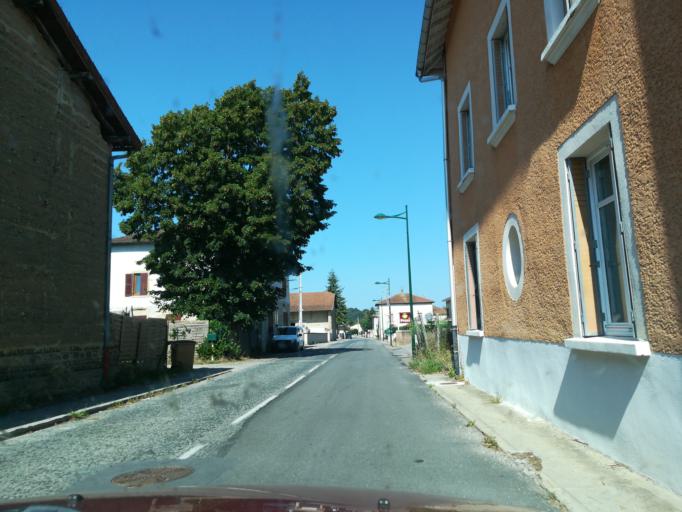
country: FR
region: Rhone-Alpes
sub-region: Departement de l'Isere
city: Charantonnay
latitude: 45.5364
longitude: 5.1088
